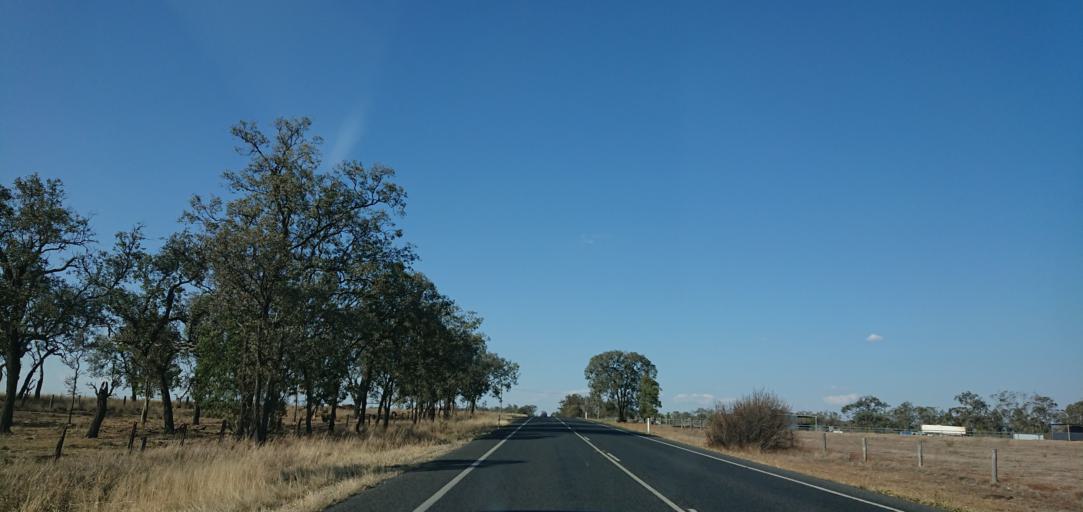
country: AU
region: Queensland
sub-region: Toowoomba
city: Westbrook
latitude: -27.6323
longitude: 151.7498
